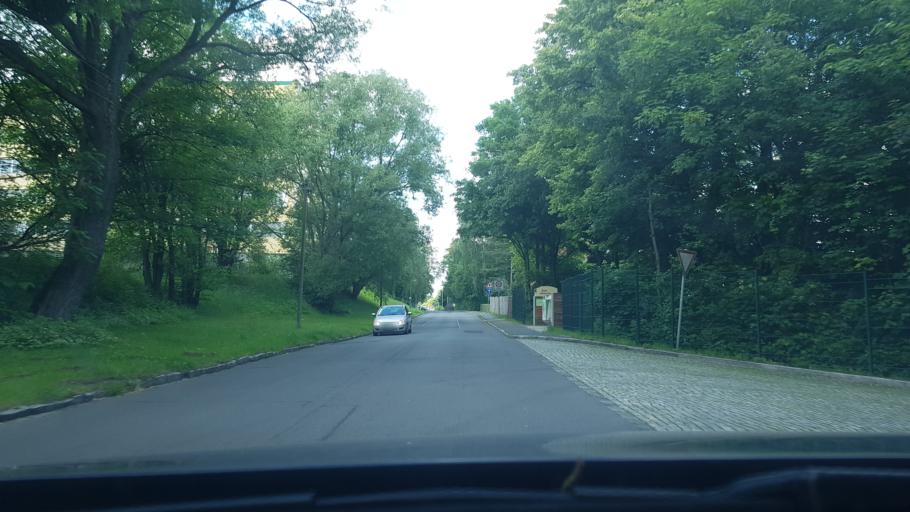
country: DE
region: Saxony
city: Bannewitz
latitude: 51.0165
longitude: 13.7093
